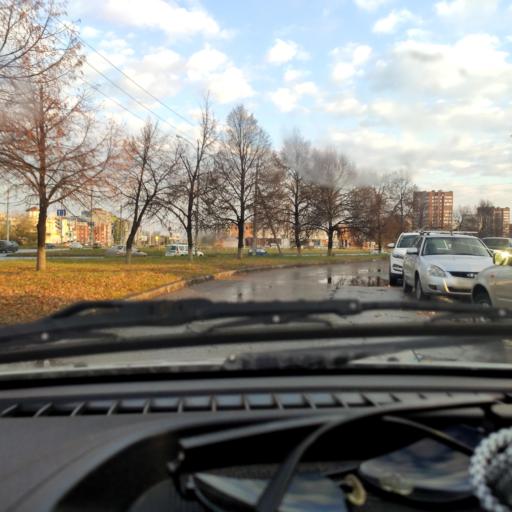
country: RU
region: Samara
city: Tol'yatti
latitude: 53.5416
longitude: 49.3160
